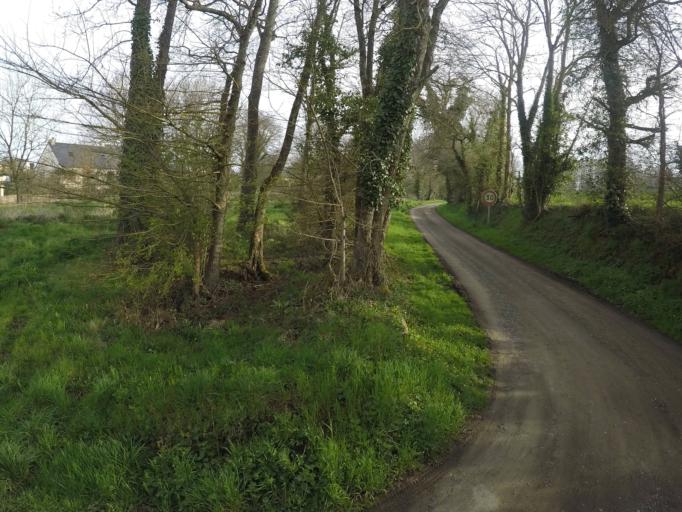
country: FR
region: Brittany
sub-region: Departement des Cotes-d'Armor
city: Lanvollon
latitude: 48.6246
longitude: -2.9914
